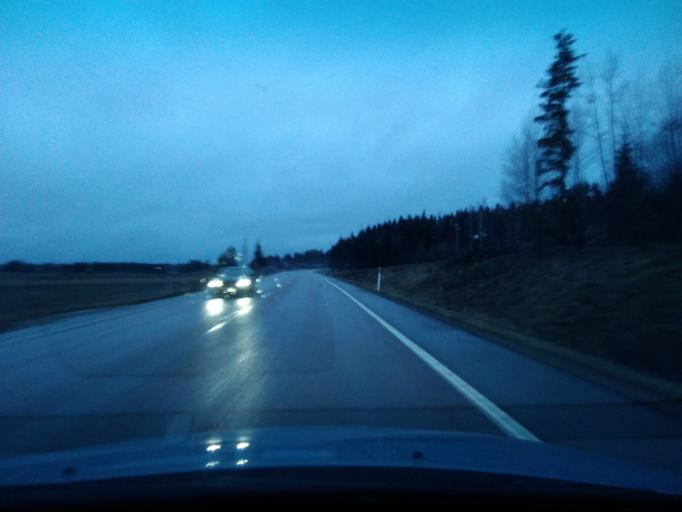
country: FI
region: Uusimaa
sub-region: Porvoo
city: Askola
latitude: 60.4840
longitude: 25.5612
